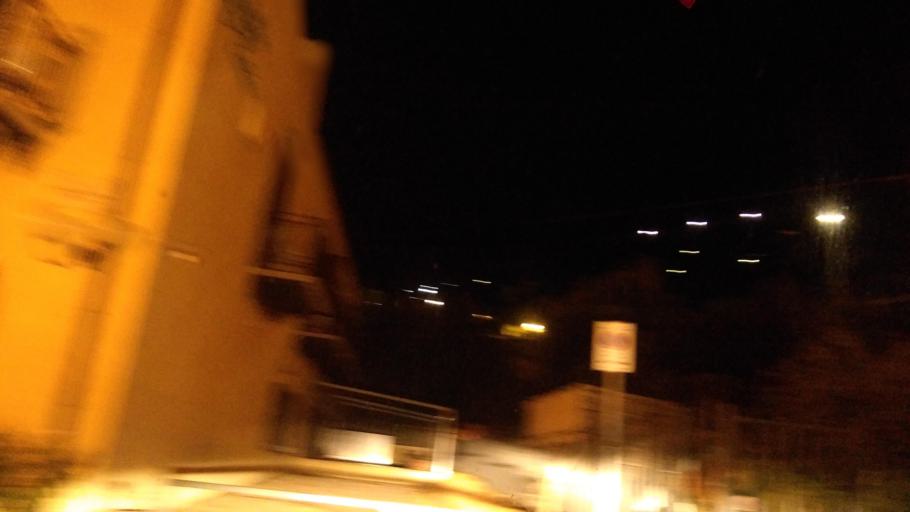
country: IT
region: Sicily
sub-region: Trapani
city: Castellammare del Golfo
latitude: 38.0285
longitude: 12.8788
